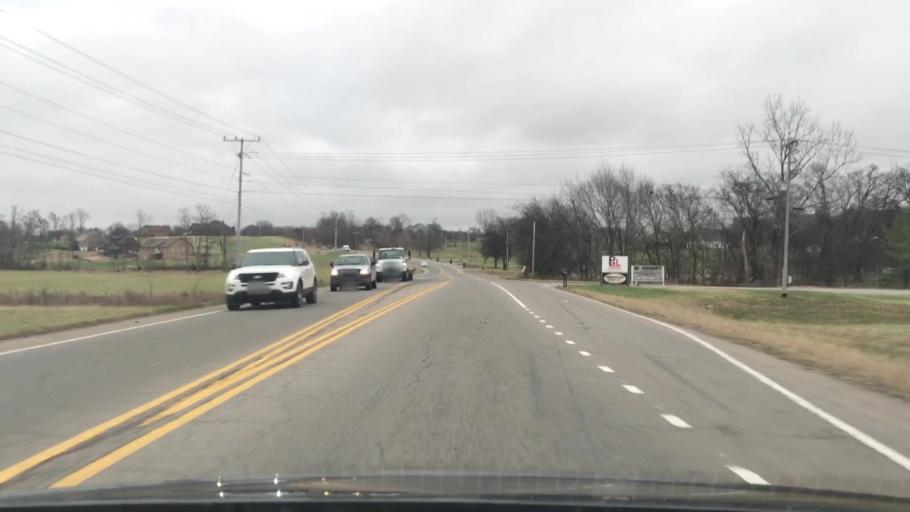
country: US
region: Kentucky
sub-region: Todd County
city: Guthrie
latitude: 36.6263
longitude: -87.2222
